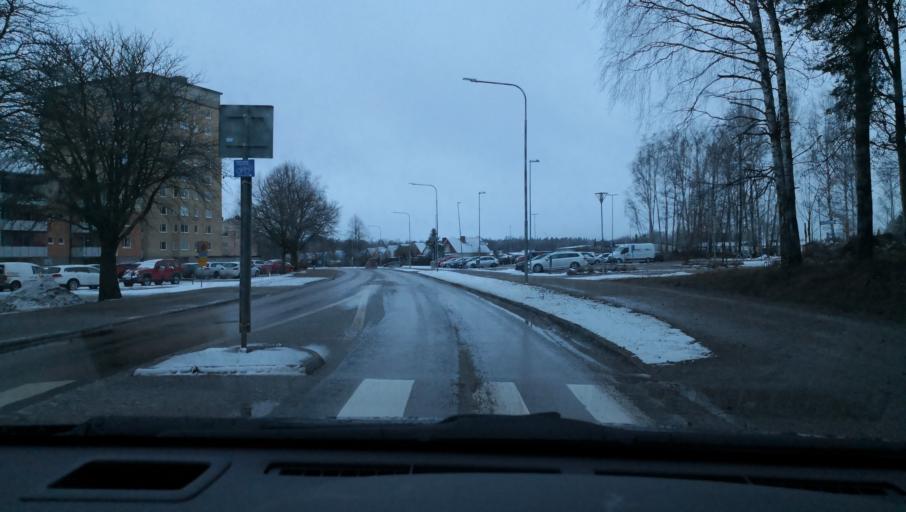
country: SE
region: Vaestmanland
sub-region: Kopings Kommun
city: Koping
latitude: 59.5234
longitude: 16.0004
